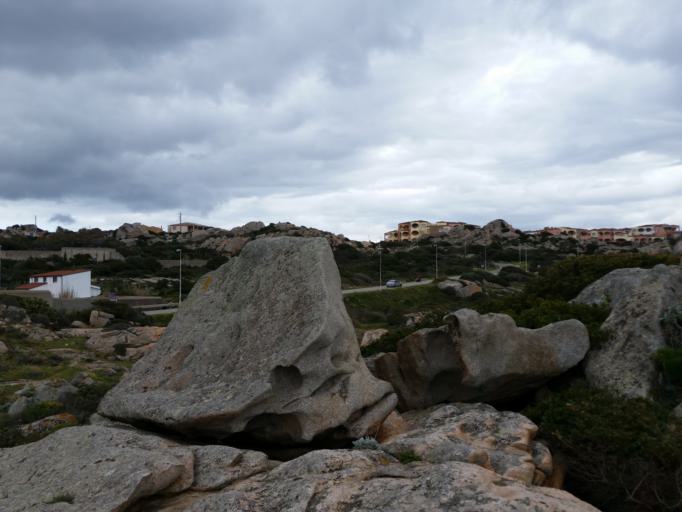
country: IT
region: Sardinia
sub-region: Provincia di Olbia-Tempio
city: La Maddalena
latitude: 41.2153
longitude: 9.3846
